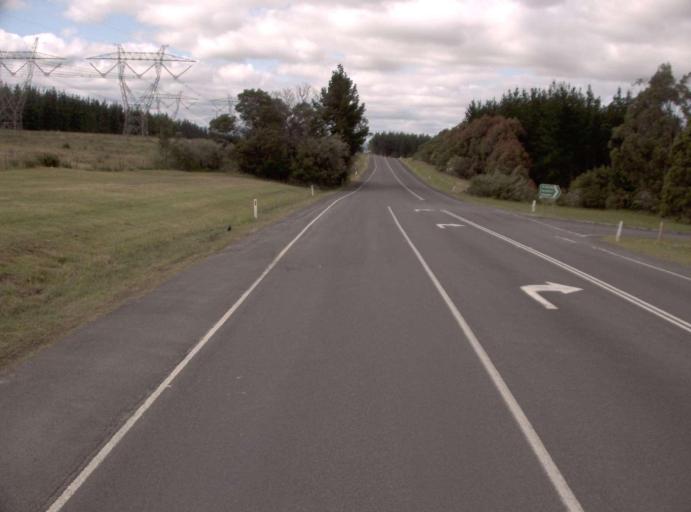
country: AU
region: Victoria
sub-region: Latrobe
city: Morwell
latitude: -38.1910
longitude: 146.4508
